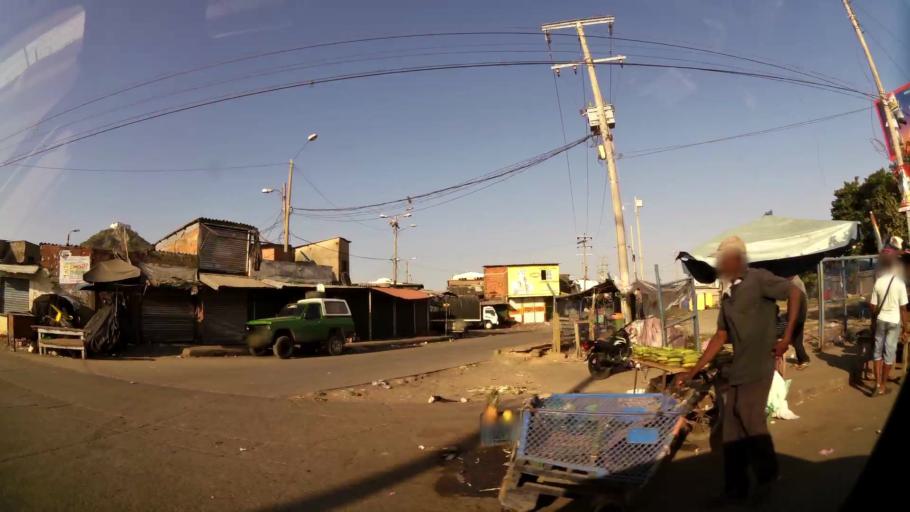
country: CO
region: Bolivar
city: Cartagena
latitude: 10.4111
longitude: -75.5246
